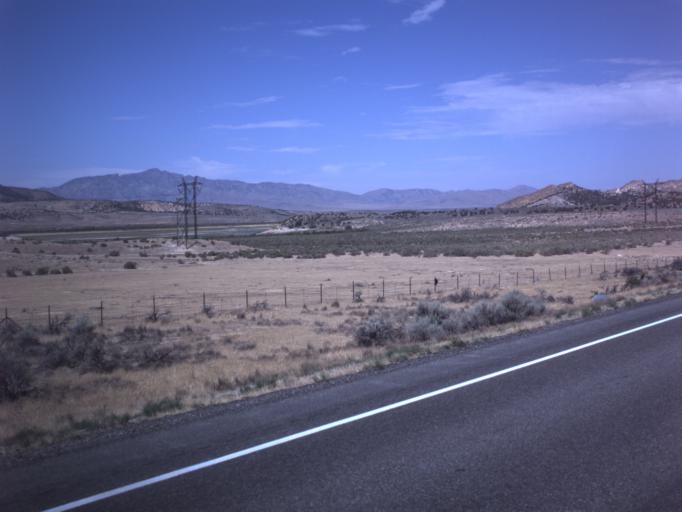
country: US
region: Utah
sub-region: Sanpete County
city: Gunnison
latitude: 39.3436
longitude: -111.9237
